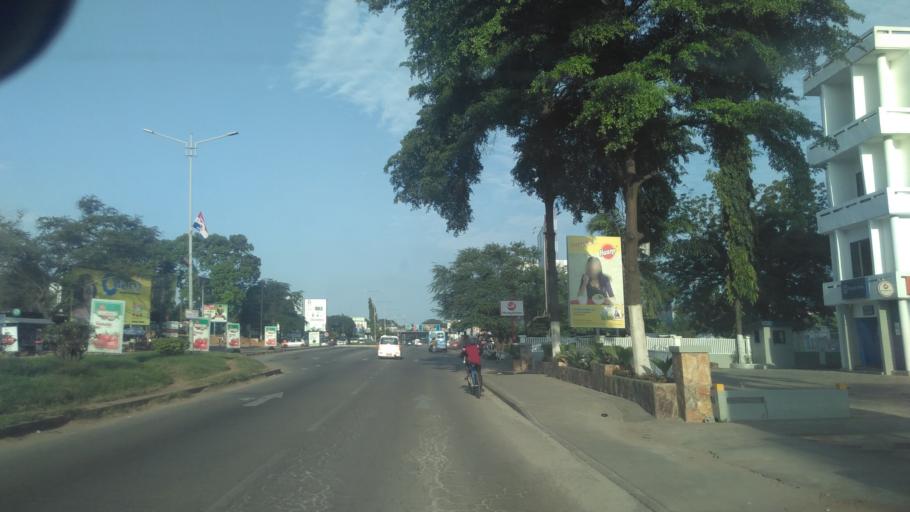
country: GH
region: Greater Accra
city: Accra
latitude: 5.5729
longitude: -0.2018
